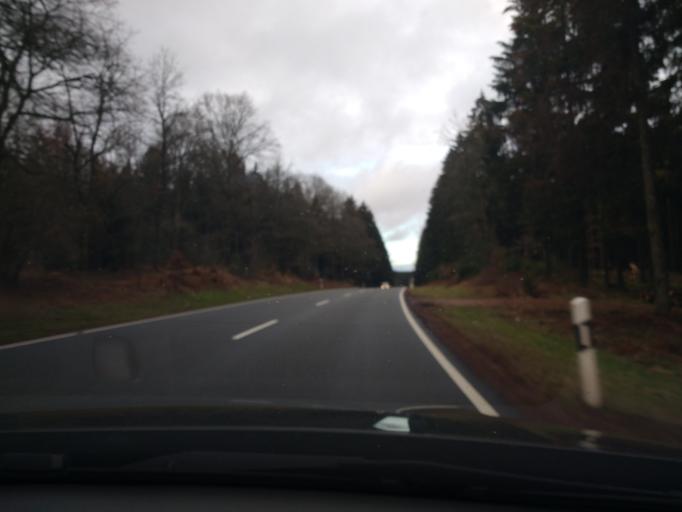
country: DE
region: Rheinland-Pfalz
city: Kell
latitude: 49.6540
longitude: 6.8530
